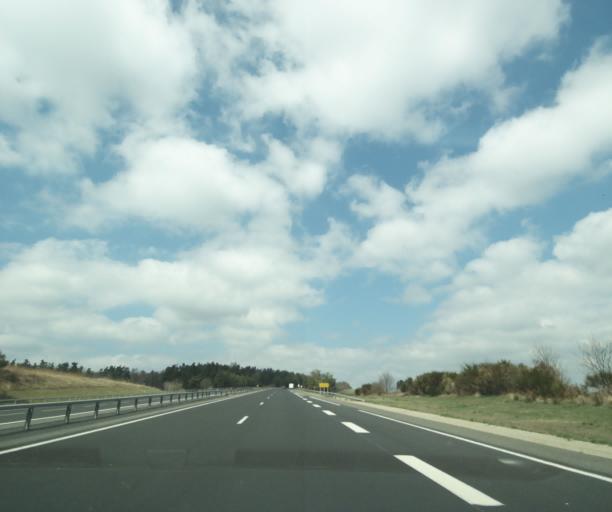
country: FR
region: Languedoc-Roussillon
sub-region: Departement de la Lozere
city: Le Malzieu-Ville
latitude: 44.8242
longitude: 3.2668
